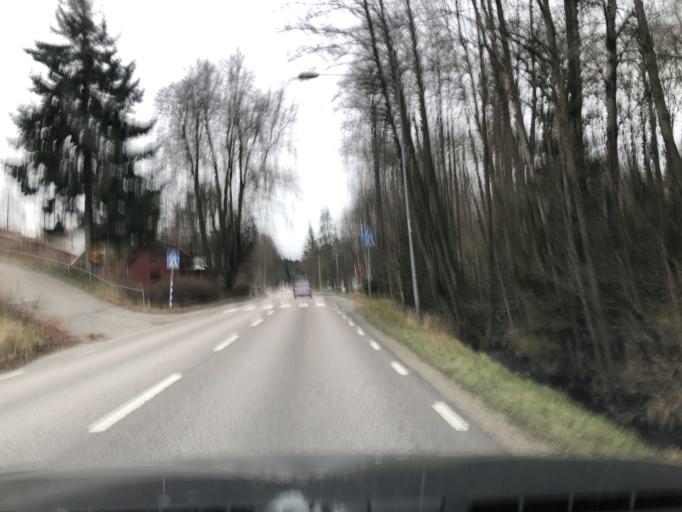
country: SE
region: Vaestra Goetaland
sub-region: Boras Kommun
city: Boras
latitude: 57.7458
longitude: 12.8907
